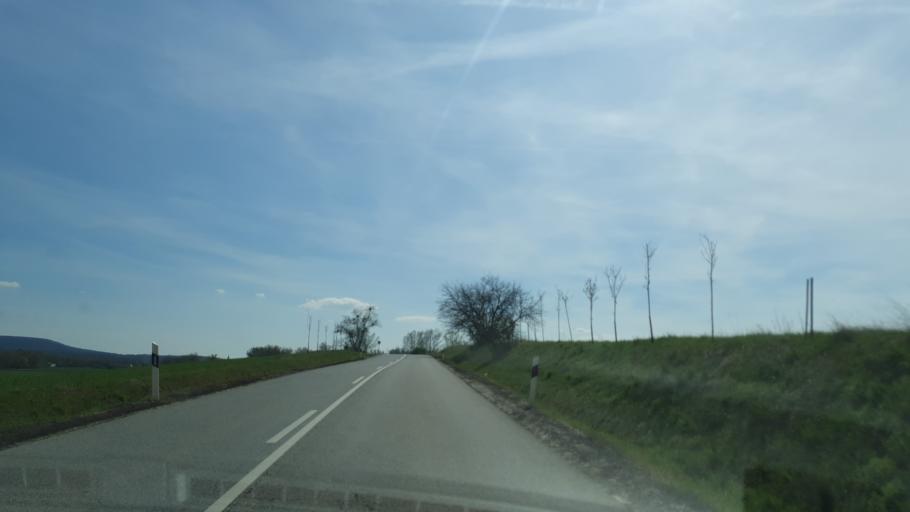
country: HU
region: Fejer
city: Pusztavam
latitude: 47.4492
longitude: 18.2369
